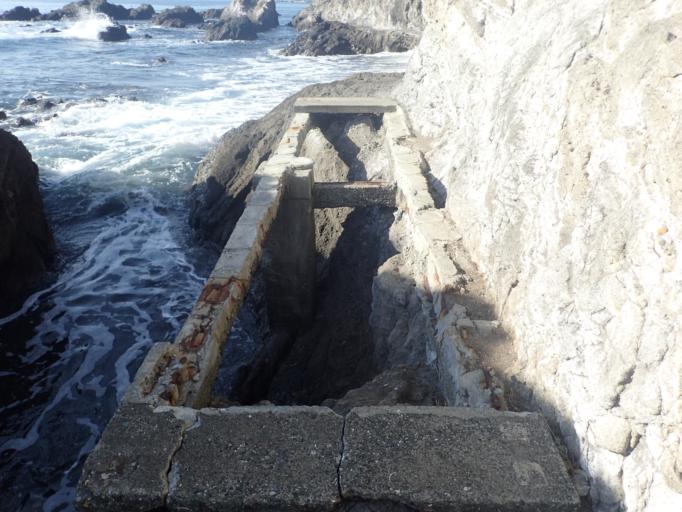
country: JP
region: Kanagawa
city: Miura
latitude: 35.1912
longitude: 139.6093
